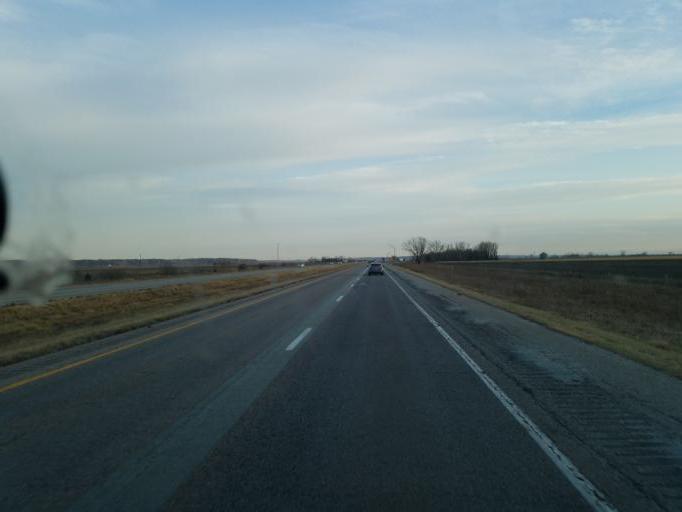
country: US
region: Iowa
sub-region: Harrison County
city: Missouri Valley
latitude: 41.5968
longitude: -95.9585
